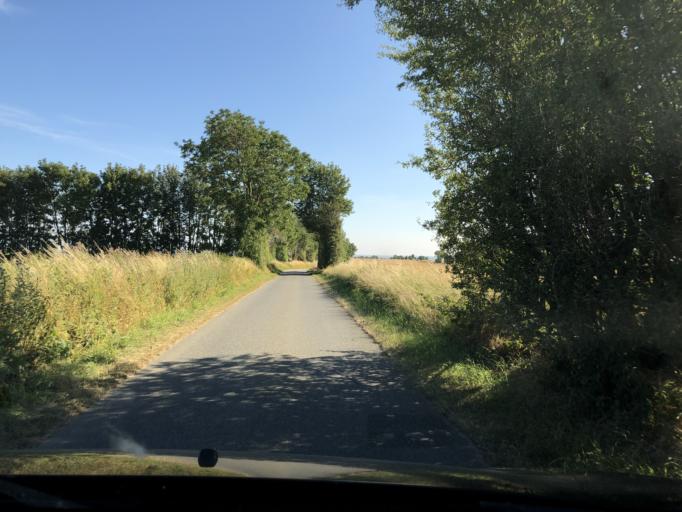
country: DK
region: South Denmark
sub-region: AEro Kommune
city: AEroskobing
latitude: 54.8570
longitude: 10.3794
